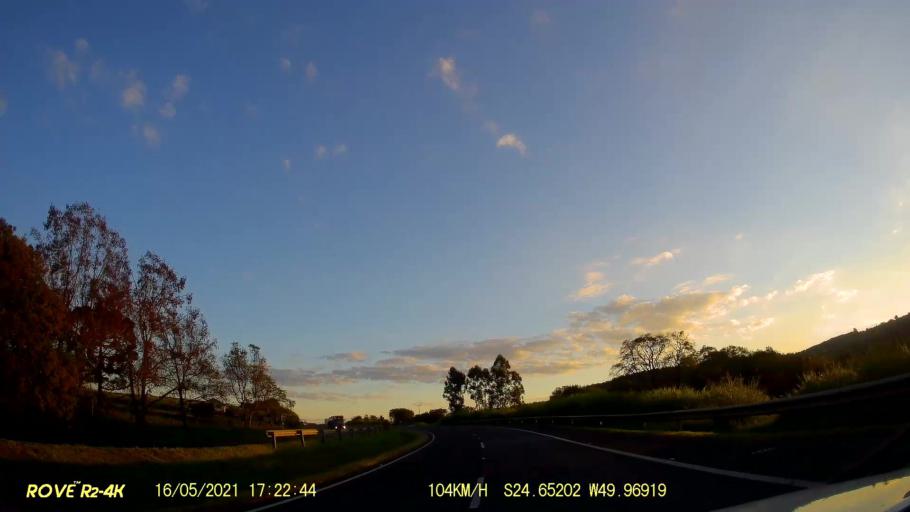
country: BR
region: Parana
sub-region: Pirai Do Sul
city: Pirai do Sul
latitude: -24.6521
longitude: -49.9695
